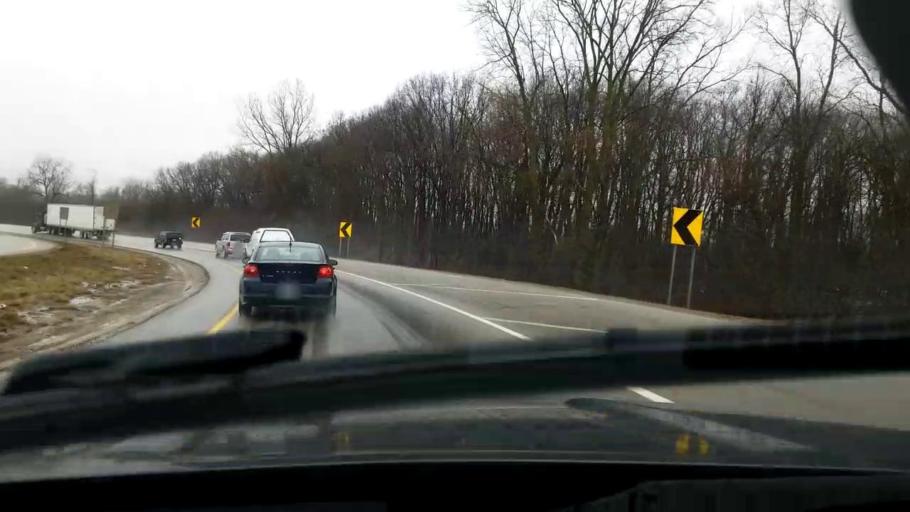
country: US
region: Michigan
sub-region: Jackson County
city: Jackson
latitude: 42.2789
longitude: -84.3593
